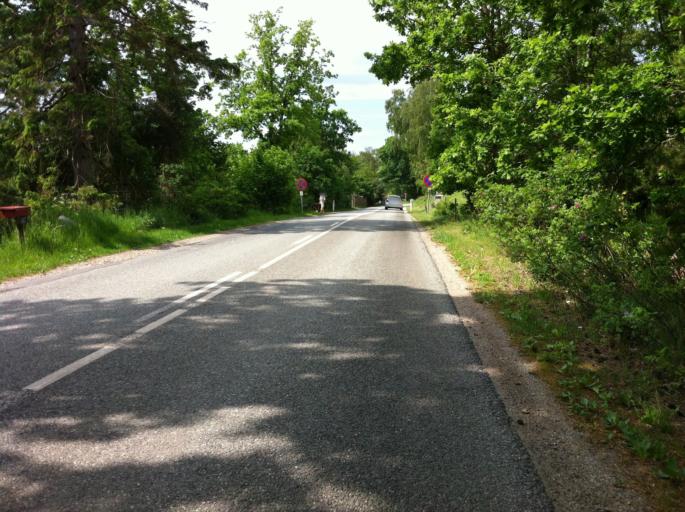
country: DK
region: Capital Region
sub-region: Gribskov Kommune
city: Helsinge
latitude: 56.1067
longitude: 12.1873
